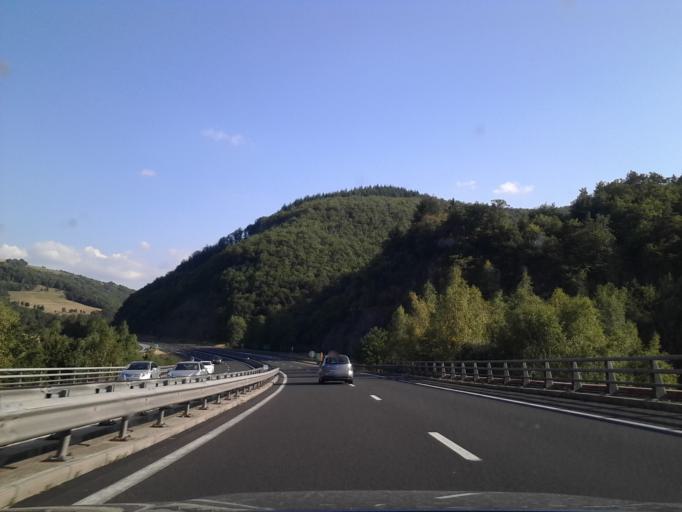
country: FR
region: Auvergne
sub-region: Departement du Cantal
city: Massiac
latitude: 45.2423
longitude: 3.2039
